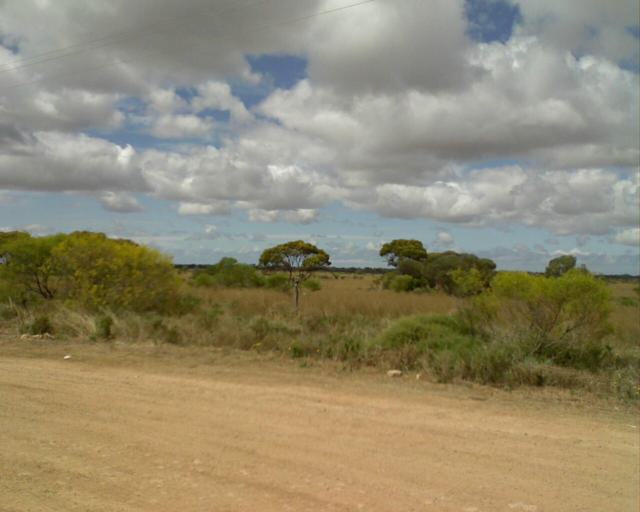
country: AU
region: South Australia
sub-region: Ceduna
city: Ceduna
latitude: -31.9509
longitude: 133.4184
